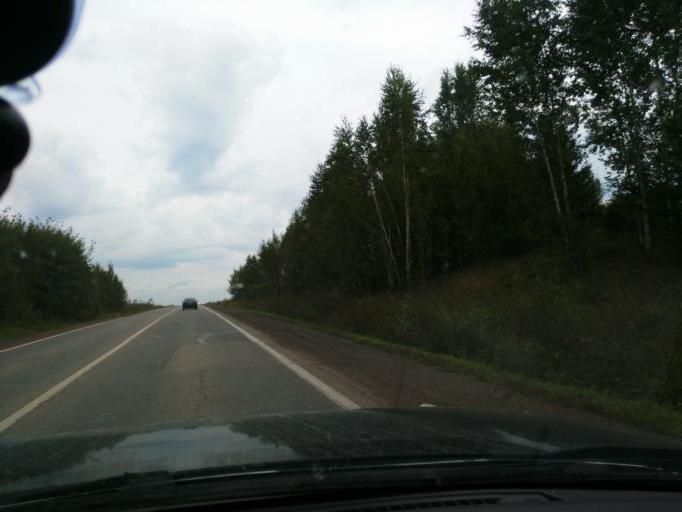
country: RU
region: Perm
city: Chernushka
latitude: 56.7113
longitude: 56.1818
